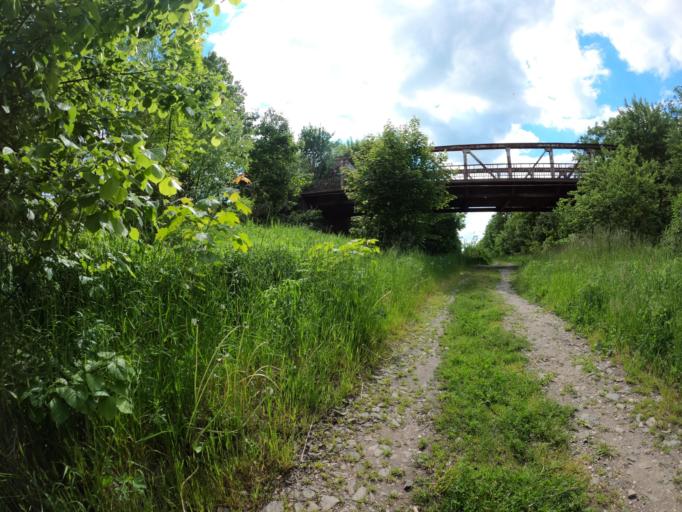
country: PL
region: Warmian-Masurian Voivodeship
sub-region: Powiat lidzbarski
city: Lidzbark Warminski
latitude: 54.1310
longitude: 20.5840
